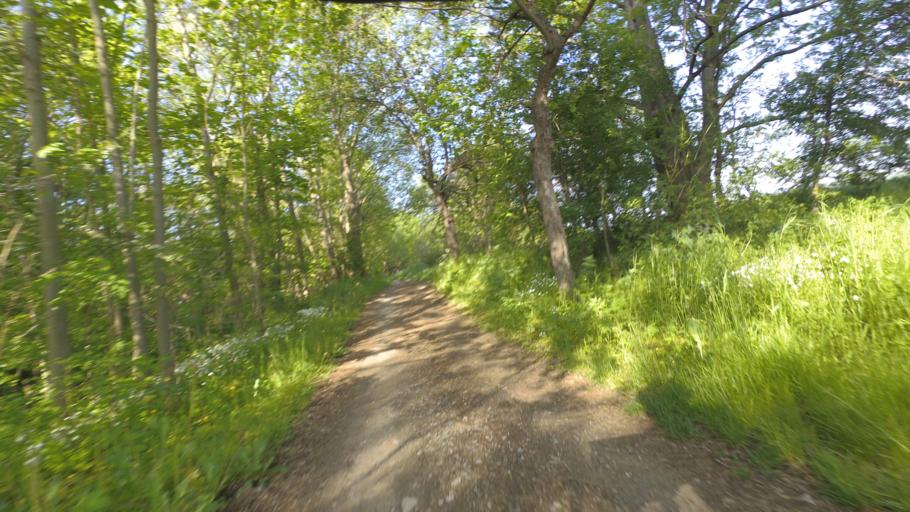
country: DE
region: Saxony-Anhalt
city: Derenburg
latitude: 51.8665
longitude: 10.8688
